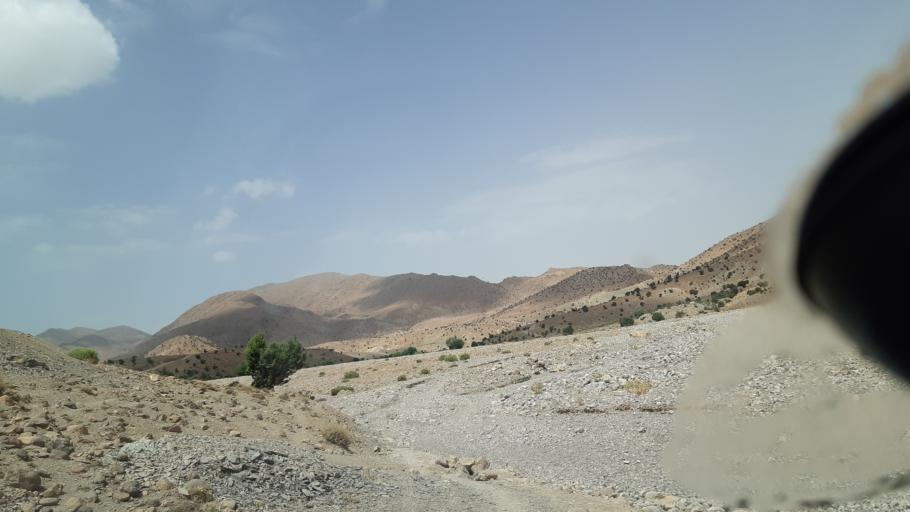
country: MA
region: Meknes-Tafilalet
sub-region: Khenifra
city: Midelt
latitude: 32.5826
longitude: -4.7730
